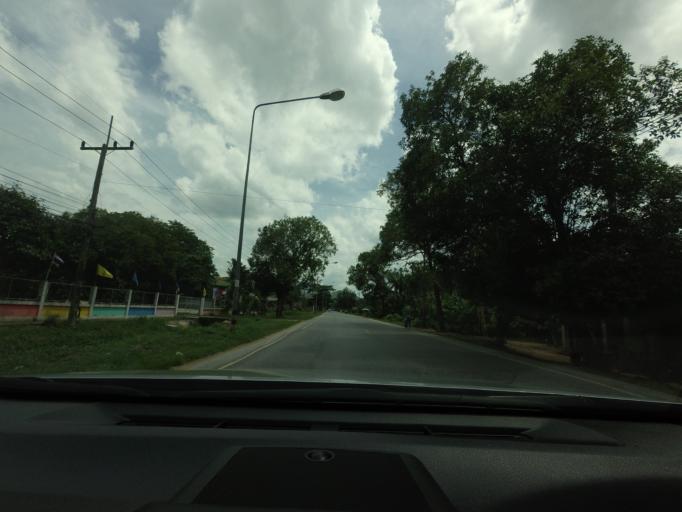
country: TH
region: Yala
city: Raman
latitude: 6.4607
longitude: 101.3689
